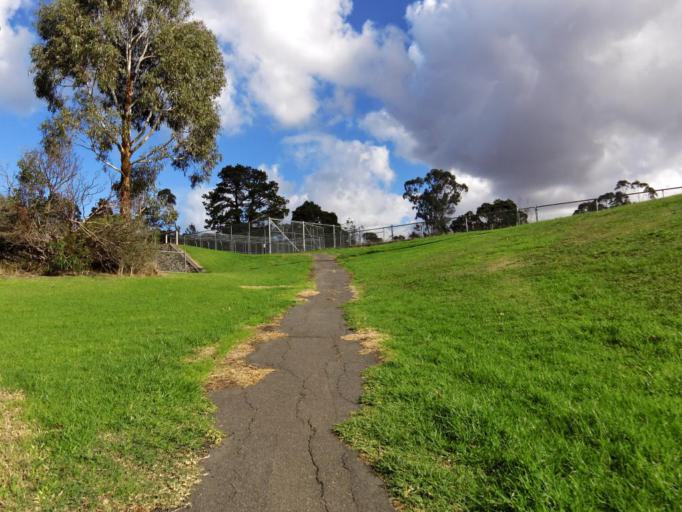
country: AU
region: Victoria
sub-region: Manningham
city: Park Orchards
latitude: -37.7749
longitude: 145.2198
